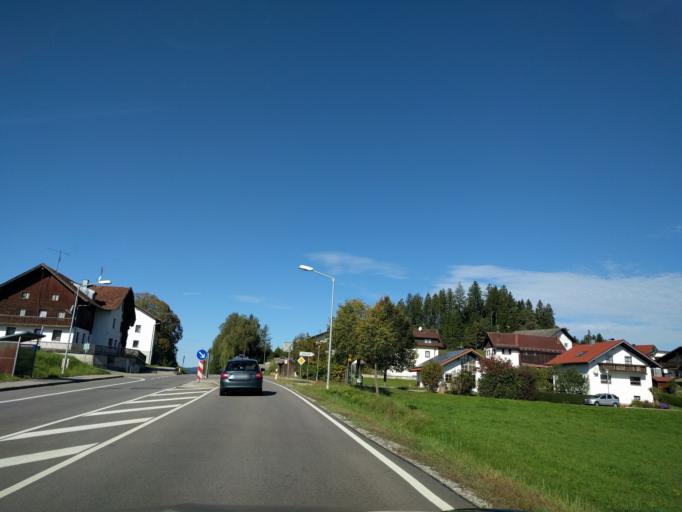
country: DE
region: Bavaria
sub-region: Lower Bavaria
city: Geiersthal
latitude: 49.0346
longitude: 12.9595
